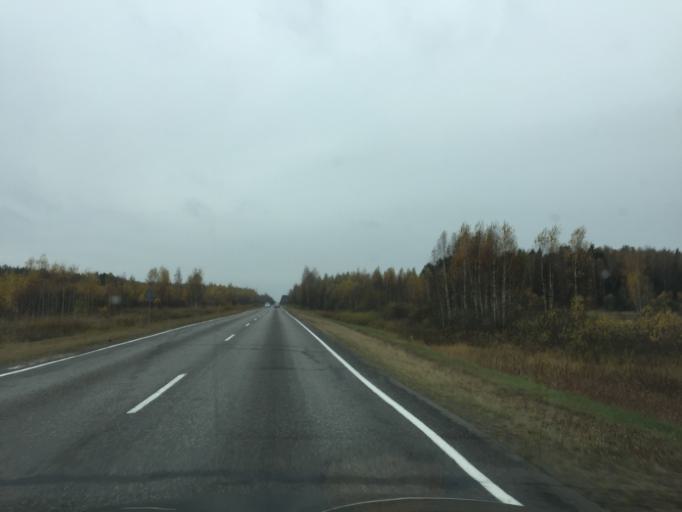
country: BY
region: Mogilev
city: Chavusy
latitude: 53.7034
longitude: 31.1494
